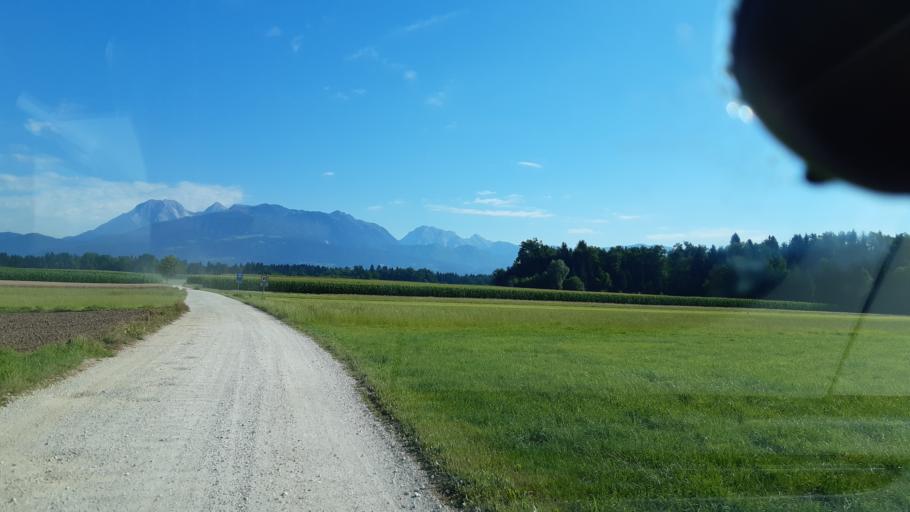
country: SI
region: Vodice
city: Vodice
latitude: 46.1864
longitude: 14.5079
